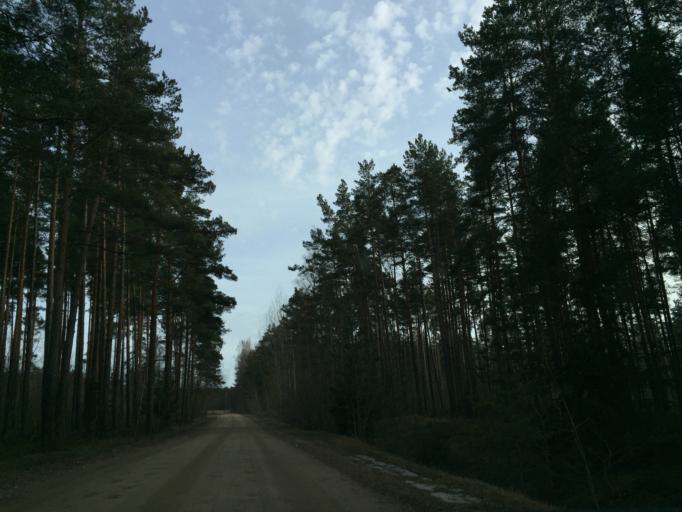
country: EE
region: Paernumaa
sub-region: Paernu linn
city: Parnu
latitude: 58.2159
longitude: 24.4960
